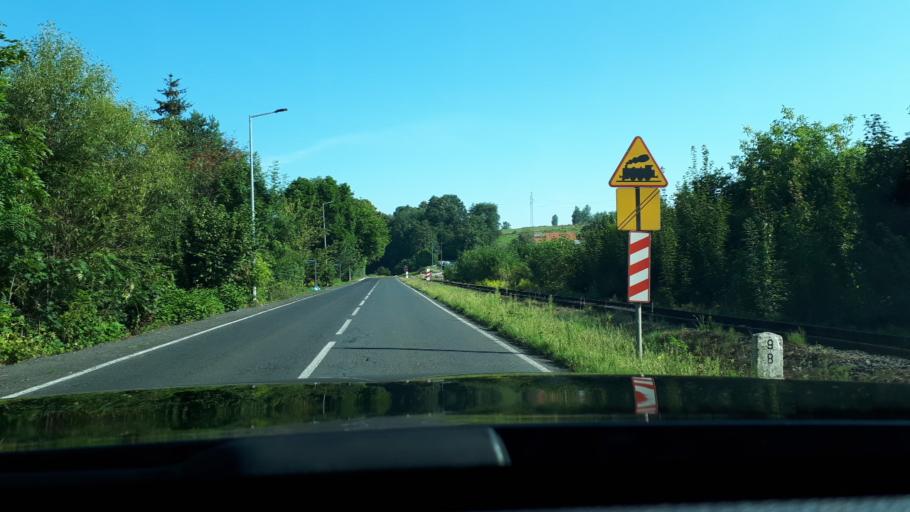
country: PL
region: Lower Silesian Voivodeship
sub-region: Powiat lubanski
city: Lesna
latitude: 51.0359
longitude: 15.2644
